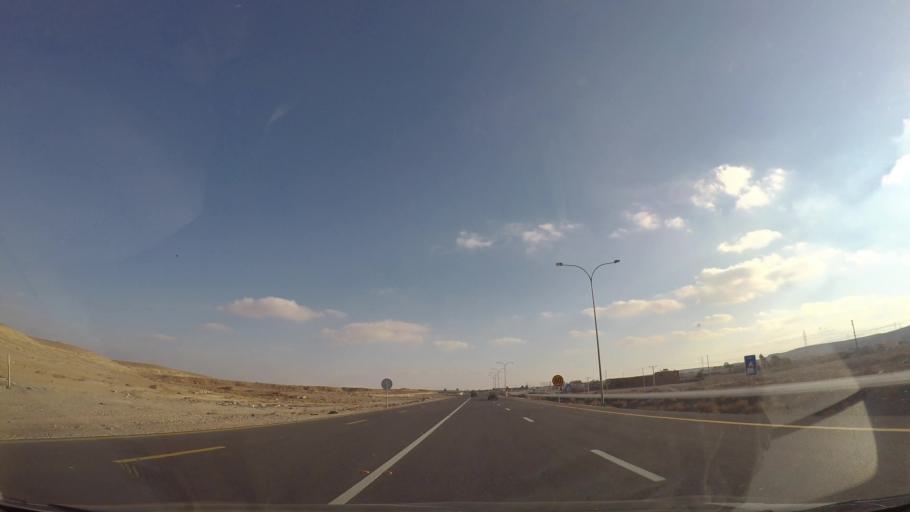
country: JO
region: Karak
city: Karak City
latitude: 31.0956
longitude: 36.0078
